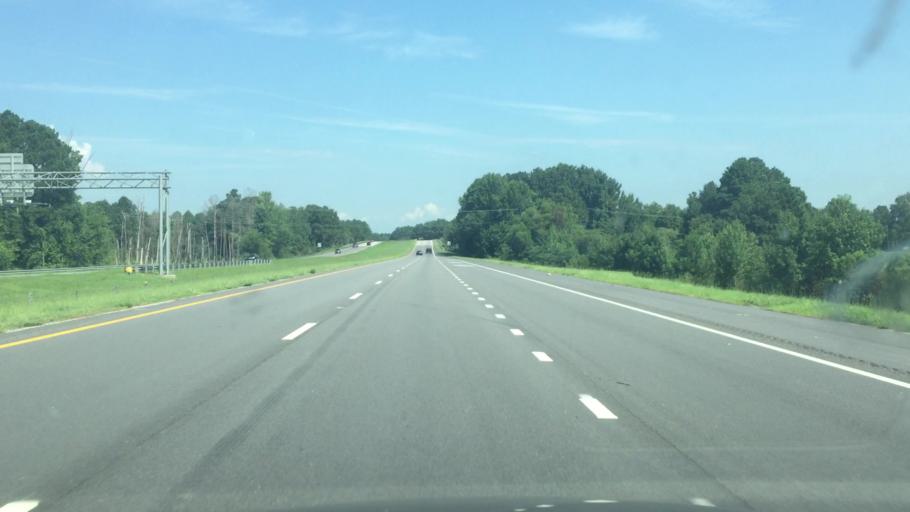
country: US
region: North Carolina
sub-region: Robeson County
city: Maxton
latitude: 34.7204
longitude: -79.3131
